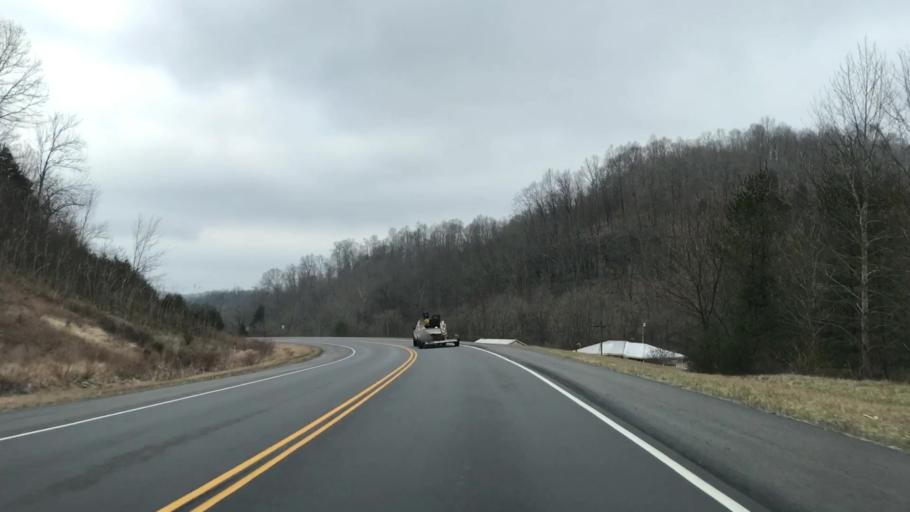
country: US
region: Kentucky
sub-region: Cumberland County
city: Burkesville
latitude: 36.8962
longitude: -85.4282
